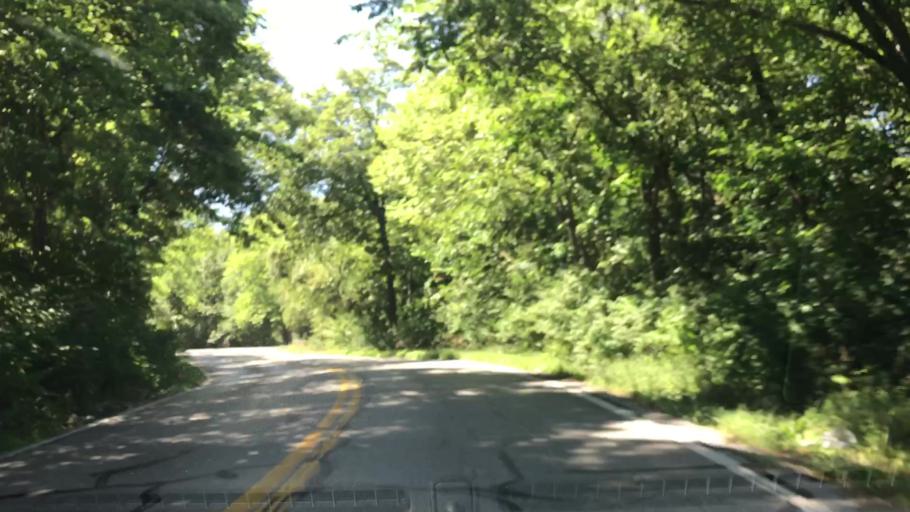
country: US
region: Missouri
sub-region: Jackson County
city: Lees Summit
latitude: 38.9281
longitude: -94.4433
